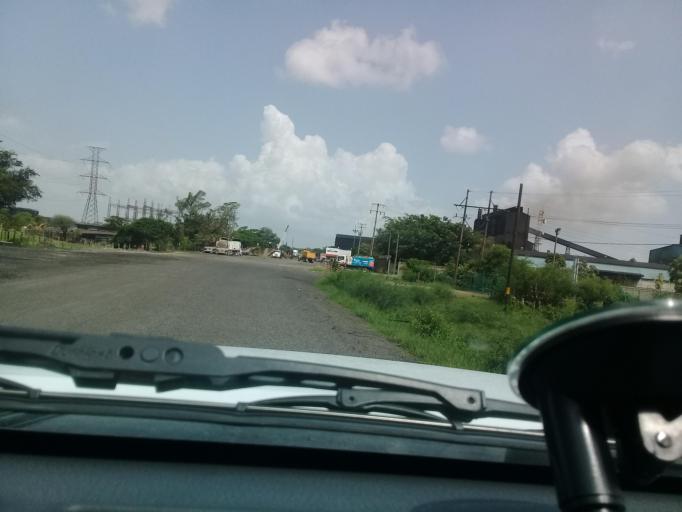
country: MX
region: Veracruz
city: Moralillo
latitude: 22.2323
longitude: -98.0206
